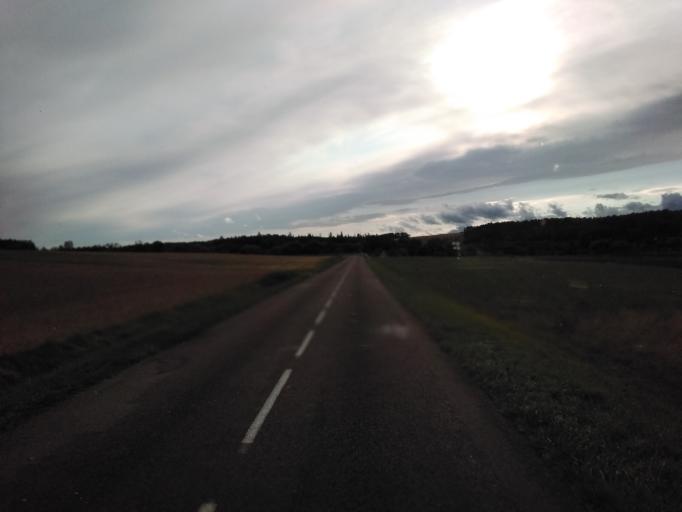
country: FR
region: Champagne-Ardenne
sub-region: Departement de l'Aube
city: Les Riceys
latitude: 47.9287
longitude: 4.3494
